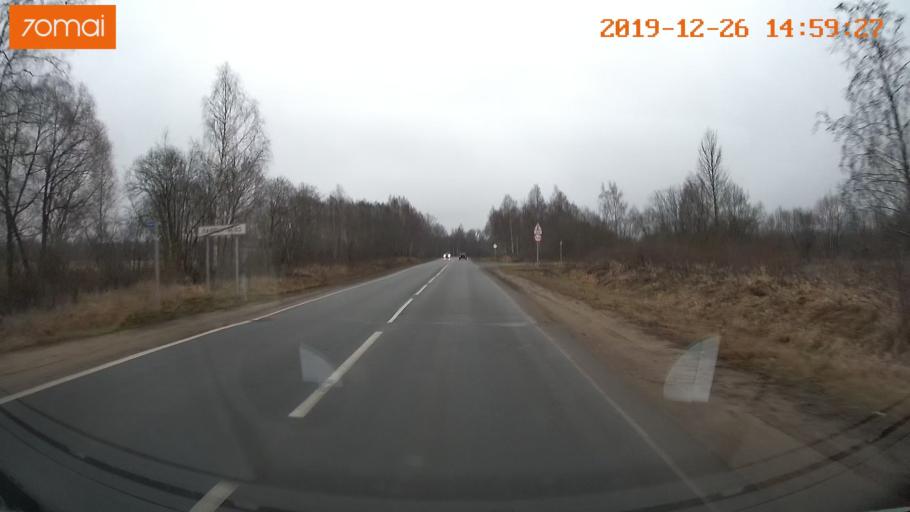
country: RU
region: Jaroslavl
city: Rybinsk
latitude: 58.2587
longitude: 38.8478
